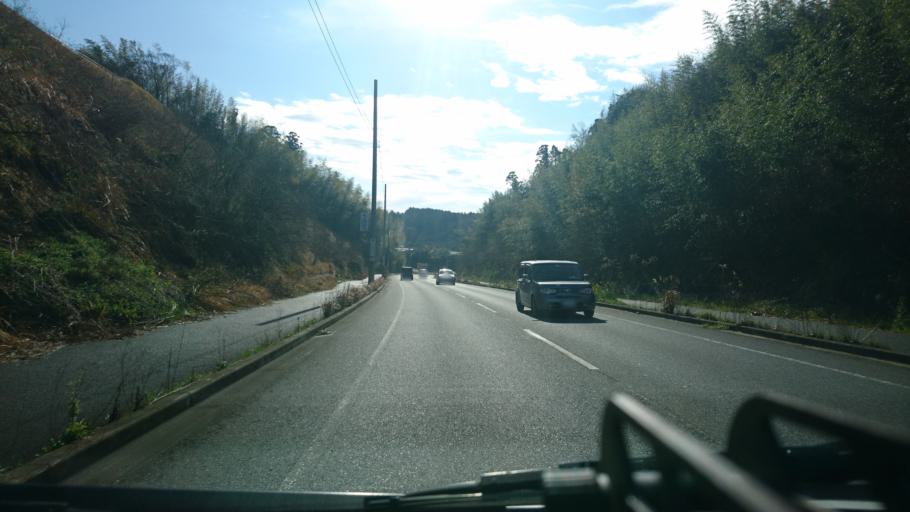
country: JP
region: Chiba
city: Kisarazu
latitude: 35.3542
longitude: 139.9397
